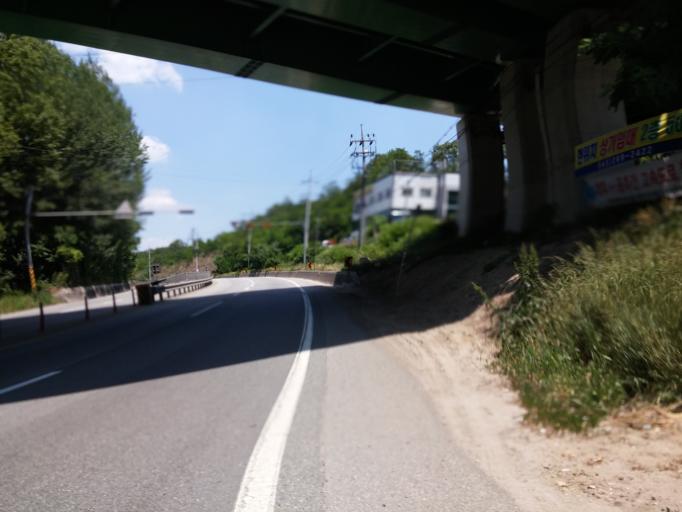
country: KR
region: Chungcheongbuk-do
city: Cheongju-si
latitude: 36.5625
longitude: 127.4489
